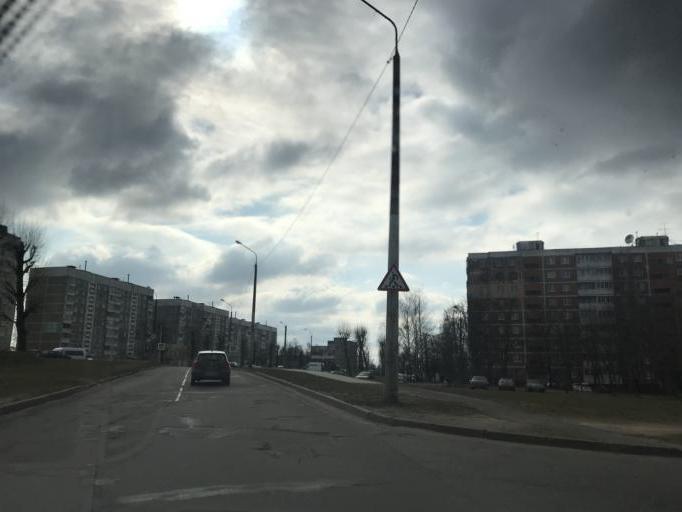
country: BY
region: Mogilev
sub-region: Mahilyowski Rayon
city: Veyno
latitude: 53.8782
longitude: 30.3813
